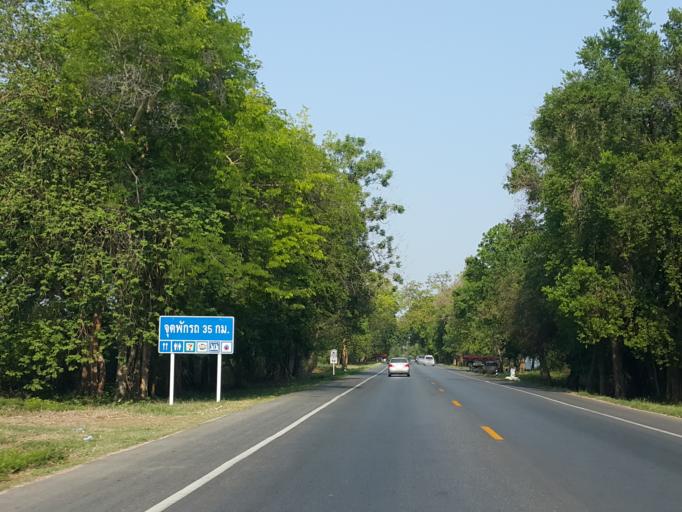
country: TH
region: Kanchanaburi
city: Sai Yok
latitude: 14.0899
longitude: 99.2997
